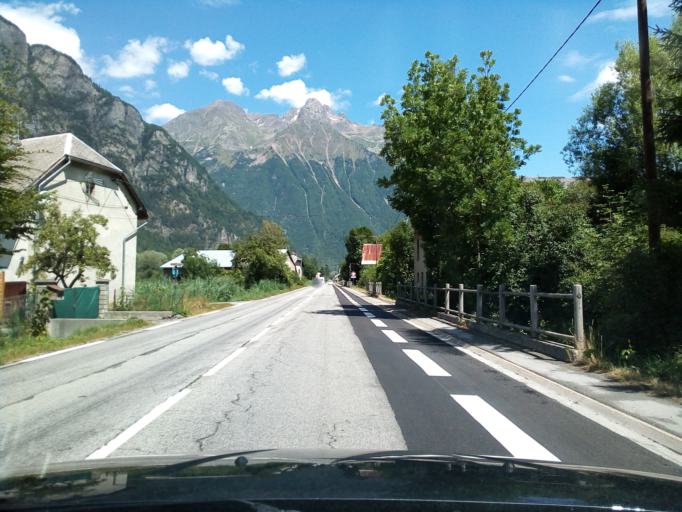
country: FR
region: Rhone-Alpes
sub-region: Departement de l'Isere
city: Huez
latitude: 45.0937
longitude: 6.0107
